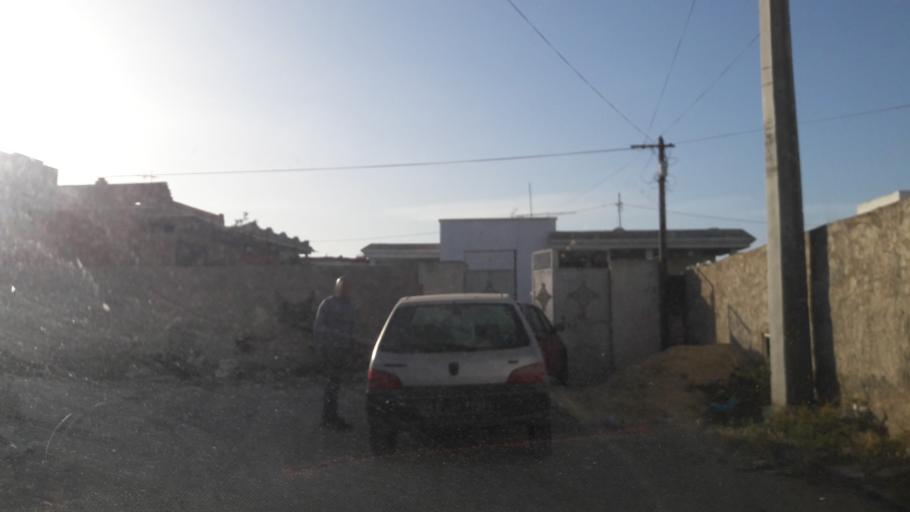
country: TN
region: Safaqis
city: Sfax
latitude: 34.8194
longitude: 10.7411
